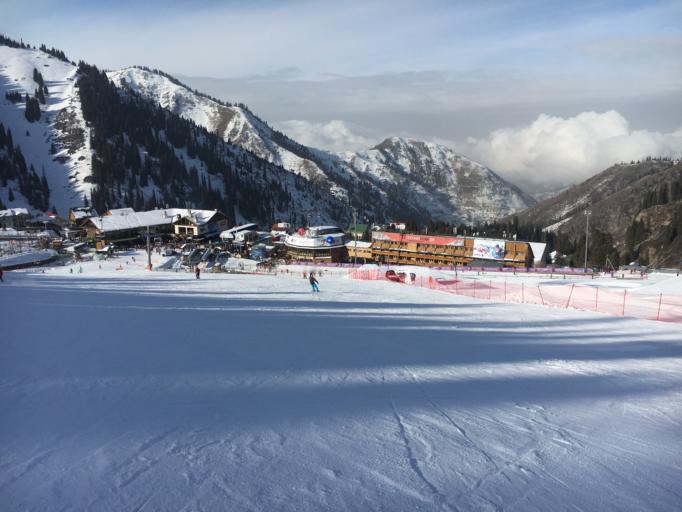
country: KZ
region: Almaty Qalasy
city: Almaty
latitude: 43.1267
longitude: 77.0842
